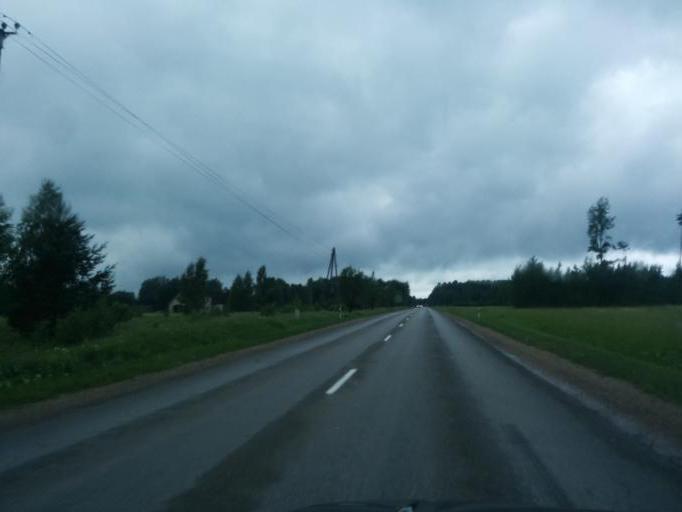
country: LV
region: Smiltene
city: Smiltene
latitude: 57.3946
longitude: 25.9663
